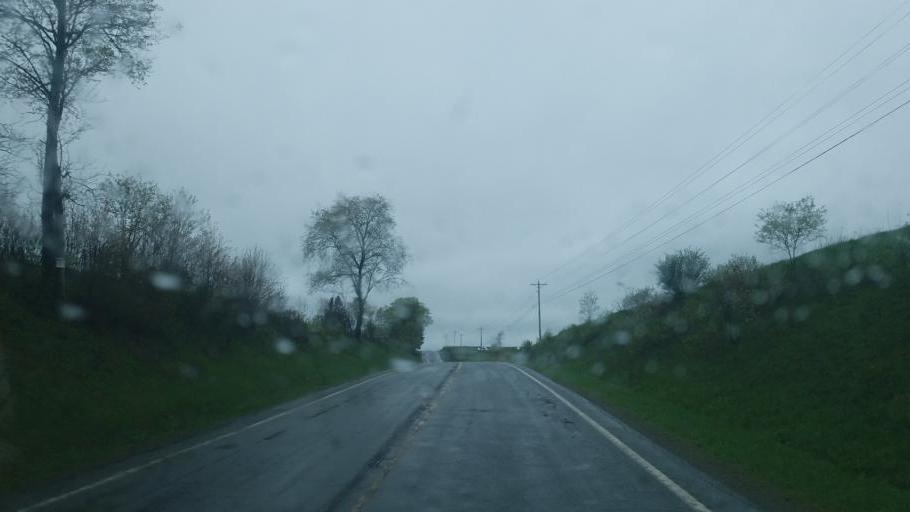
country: US
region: Pennsylvania
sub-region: Potter County
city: Coudersport
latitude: 41.8520
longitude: -77.8810
